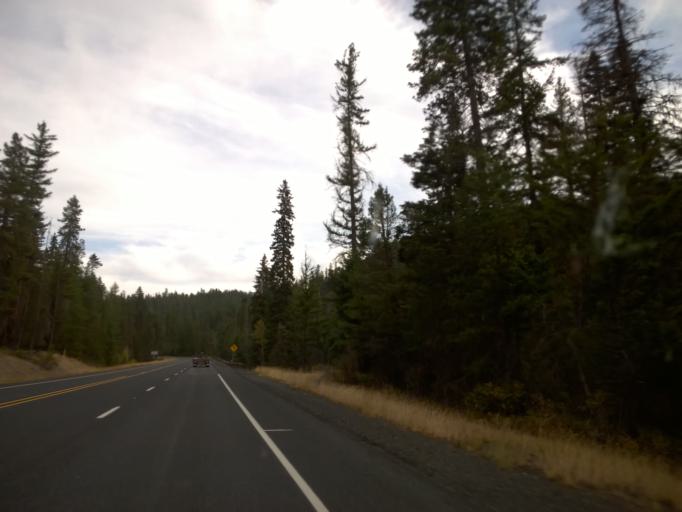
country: US
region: Washington
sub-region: Chelan County
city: Cashmere
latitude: 47.3739
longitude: -120.5862
